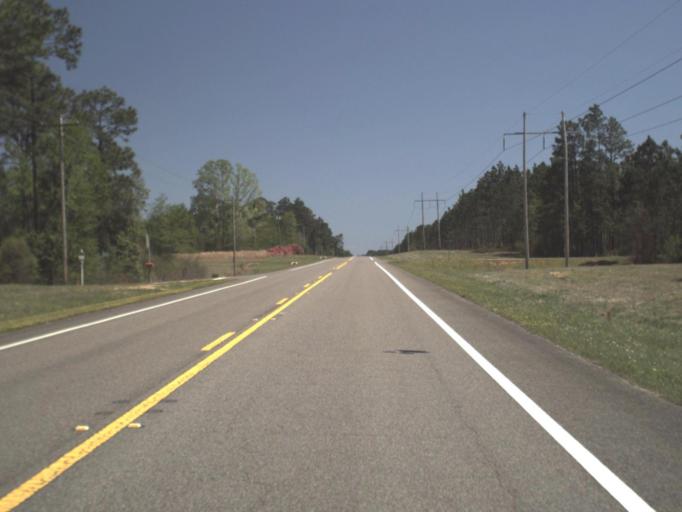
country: US
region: Florida
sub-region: Santa Rosa County
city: Point Baker
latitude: 30.8888
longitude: -86.9731
